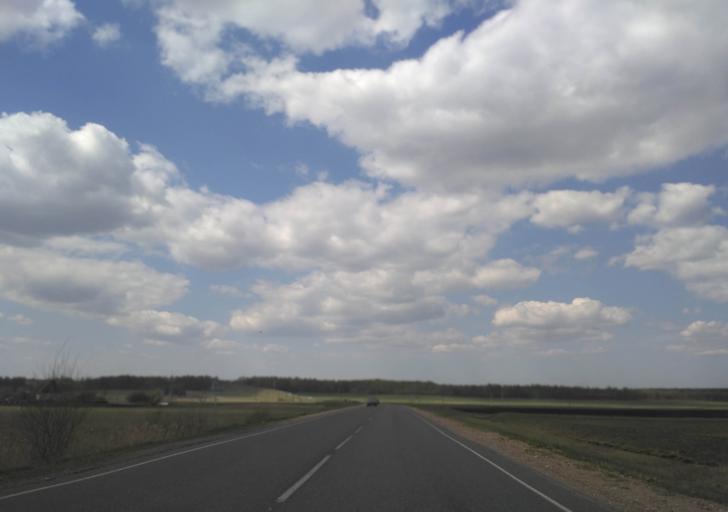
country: BY
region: Minsk
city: Vilyeyka
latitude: 54.5198
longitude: 26.9733
